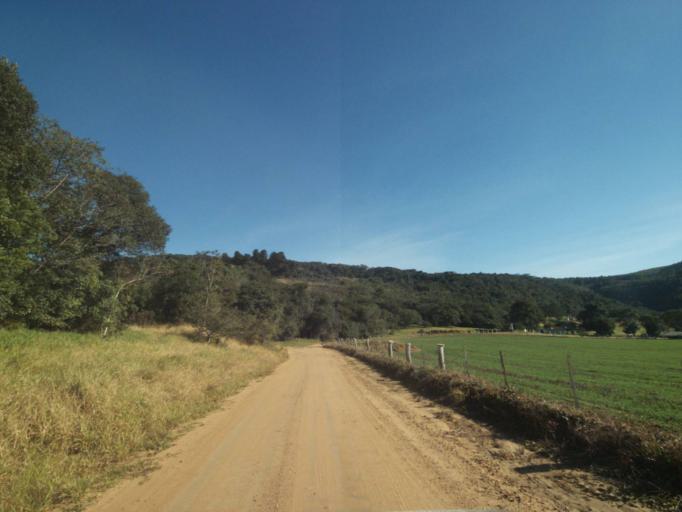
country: BR
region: Parana
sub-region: Tibagi
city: Tibagi
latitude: -24.5557
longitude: -50.5224
